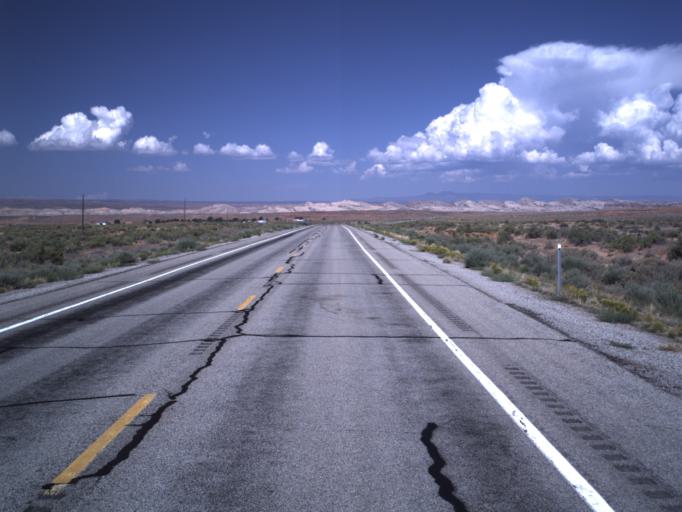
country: US
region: Utah
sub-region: San Juan County
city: Blanding
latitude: 37.1991
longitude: -109.6026
